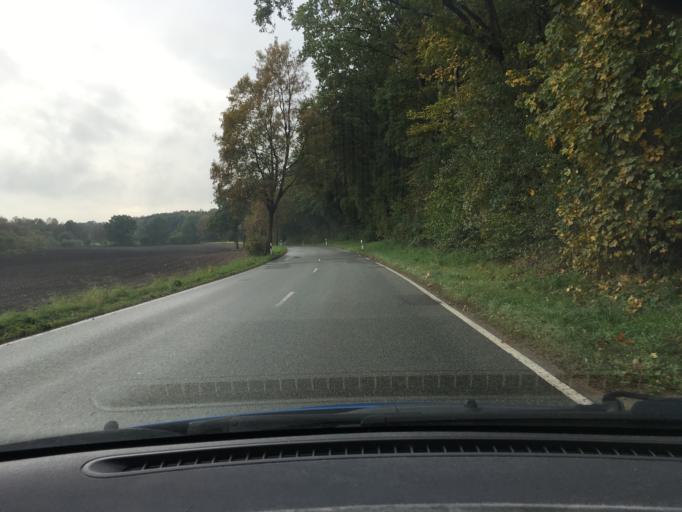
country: DE
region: Schleswig-Holstein
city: Tensfeld
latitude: 54.0383
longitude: 10.3161
